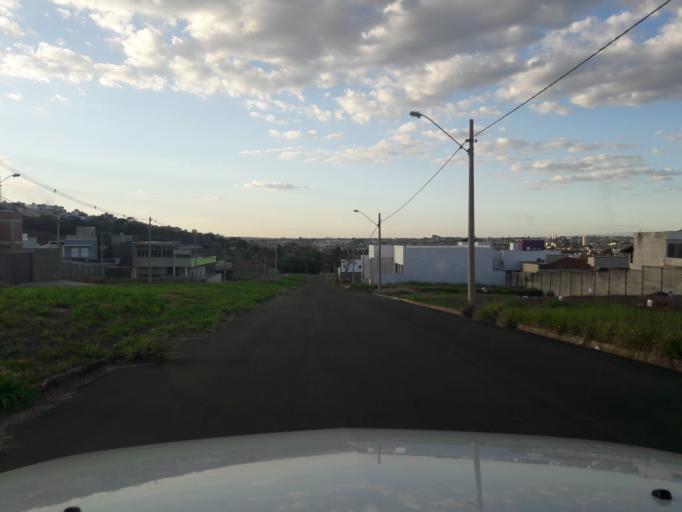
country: BR
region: Sao Paulo
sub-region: Moji-Guacu
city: Mogi-Gaucu
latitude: -22.3926
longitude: -46.9519
